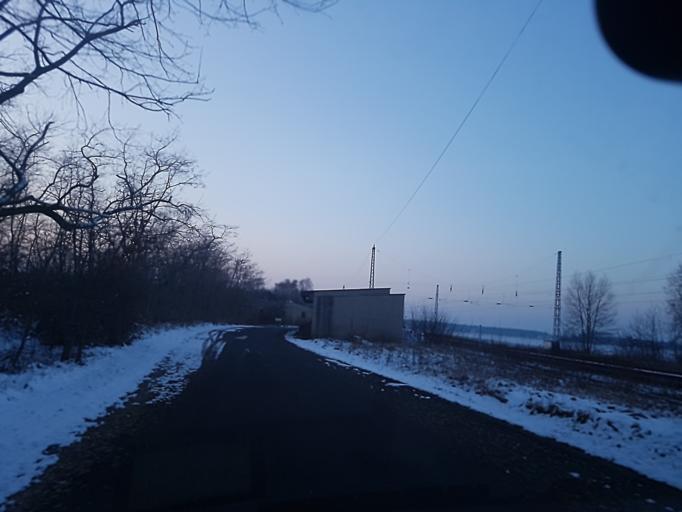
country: DE
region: Brandenburg
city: Bad Liebenwerda
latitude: 51.5378
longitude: 13.3400
